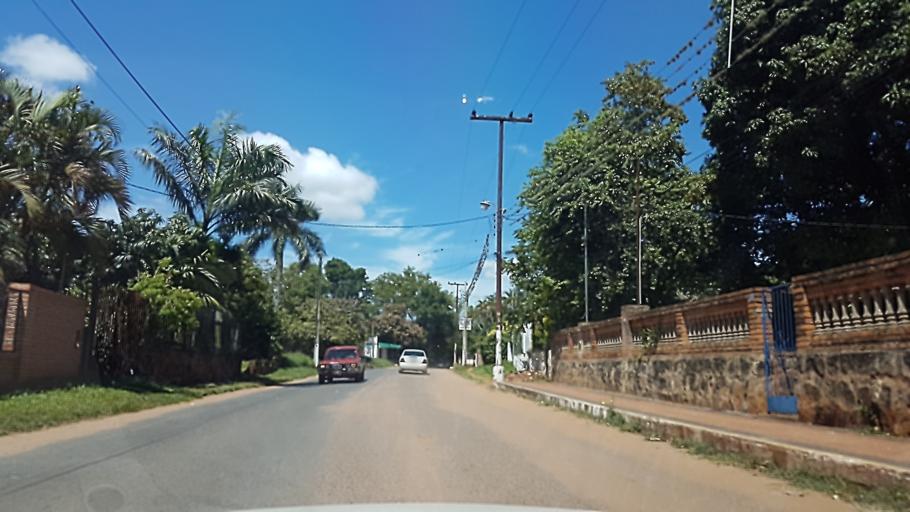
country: PY
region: Central
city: Capiata
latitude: -25.3501
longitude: -57.4334
